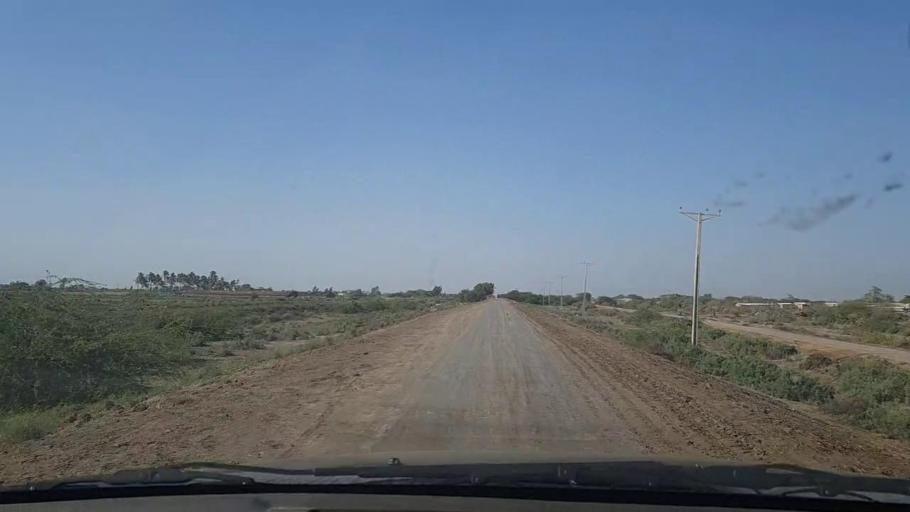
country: PK
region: Sindh
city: Chuhar Jamali
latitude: 24.2955
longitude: 67.7548
